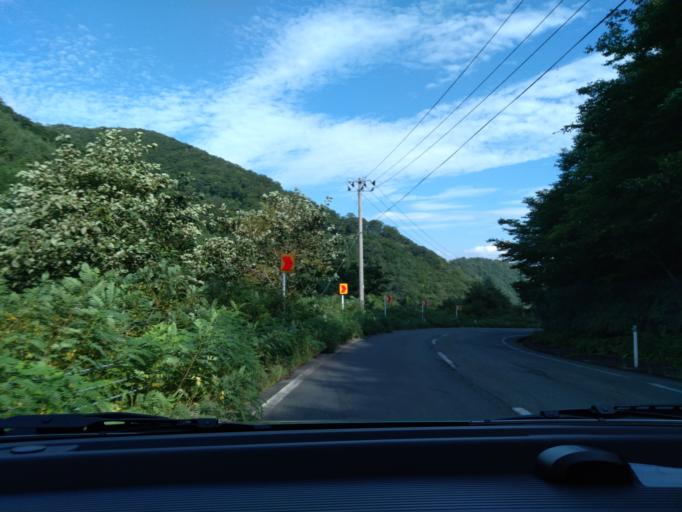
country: JP
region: Iwate
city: Shizukuishi
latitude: 39.6295
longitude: 141.0594
